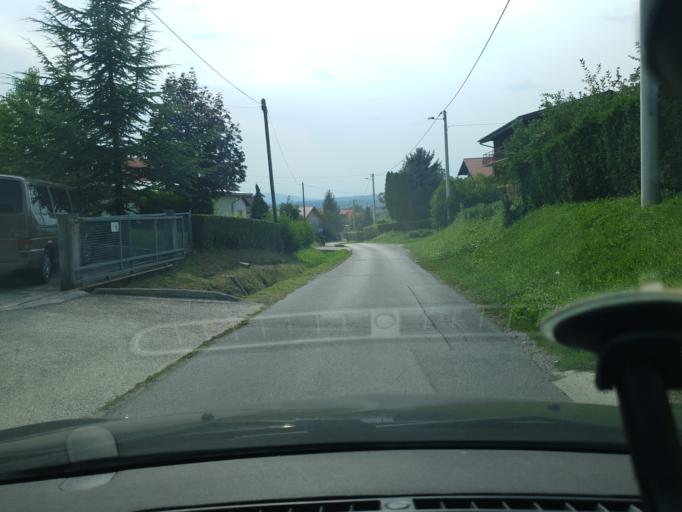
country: HR
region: Zagrebacka
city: Jablanovec
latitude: 45.8772
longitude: 15.8494
